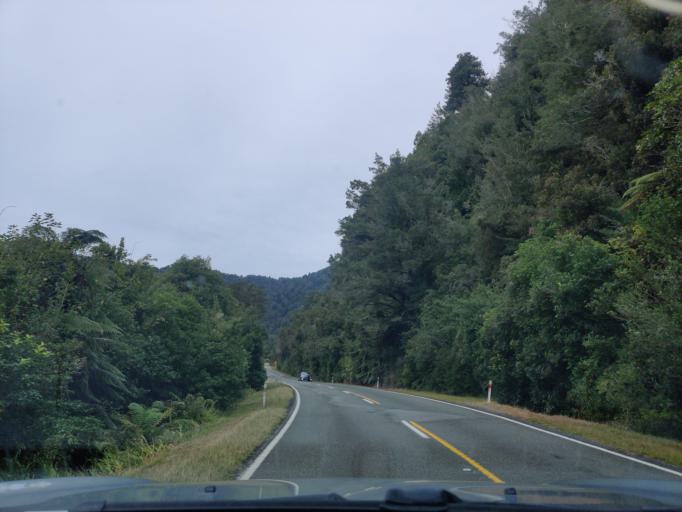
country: NZ
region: West Coast
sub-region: Buller District
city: Westport
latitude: -41.8614
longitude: 171.7713
